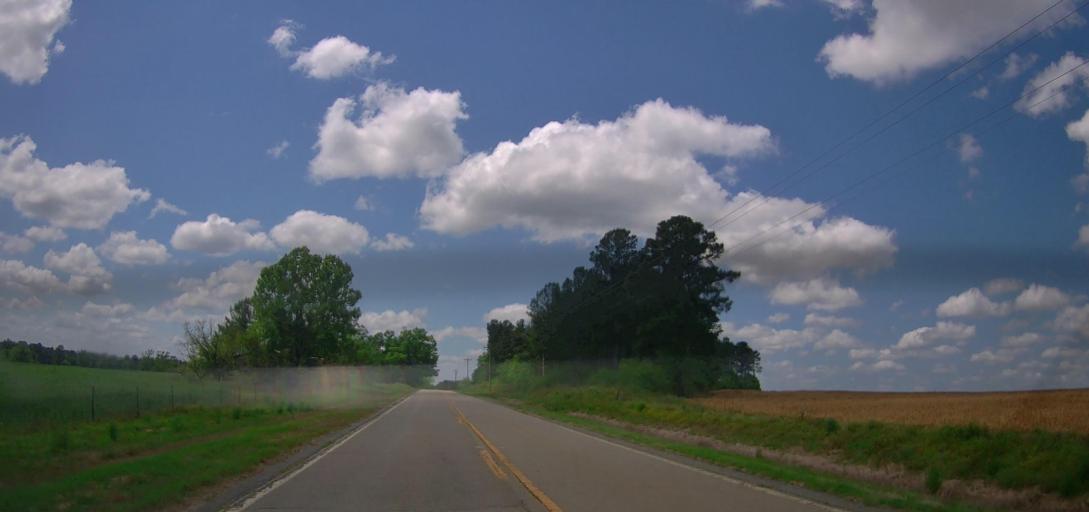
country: US
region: Georgia
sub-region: Dodge County
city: Chester
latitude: 32.5169
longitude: -83.2206
